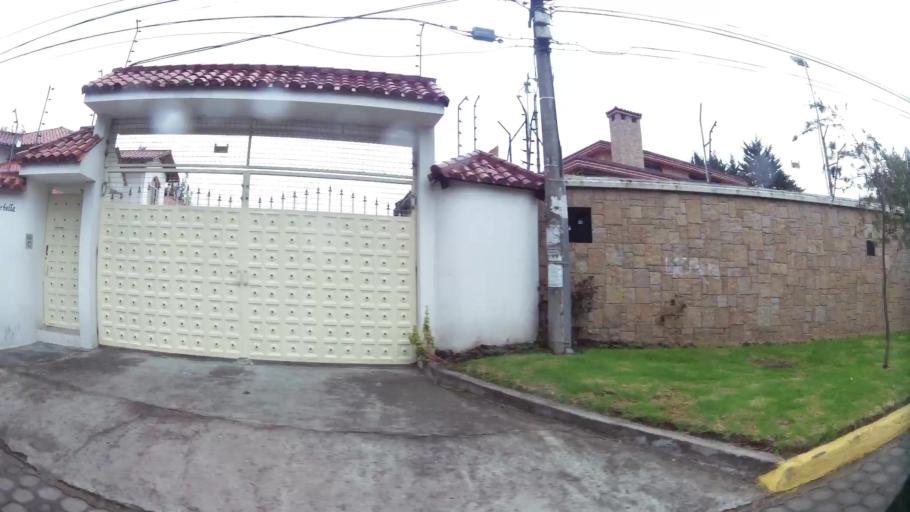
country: EC
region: Pichincha
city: Sangolqui
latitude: -0.2762
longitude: -78.4660
